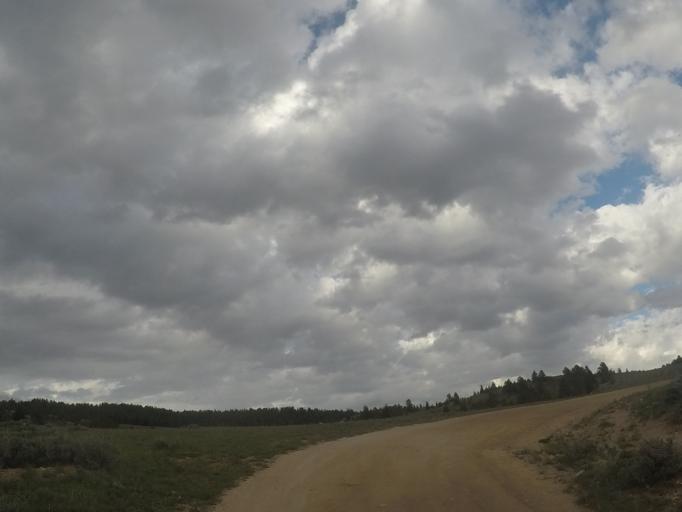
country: US
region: Wyoming
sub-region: Sheridan County
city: Sheridan
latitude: 44.5041
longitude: -107.4491
